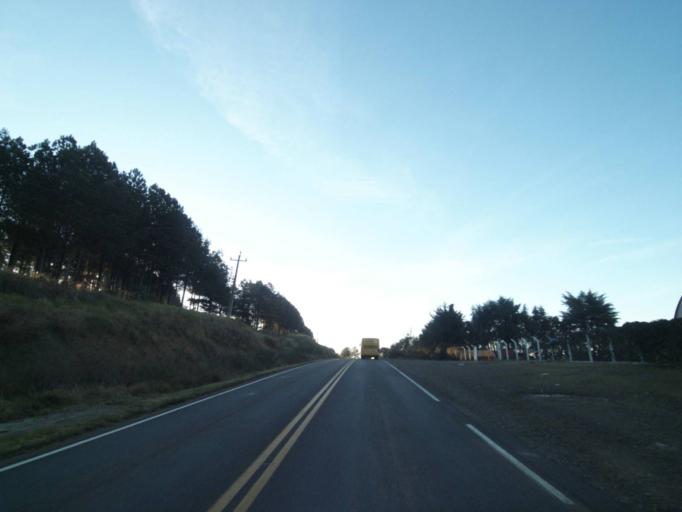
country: BR
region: Parana
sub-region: Tibagi
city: Tibagi
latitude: -24.5036
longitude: -50.4406
